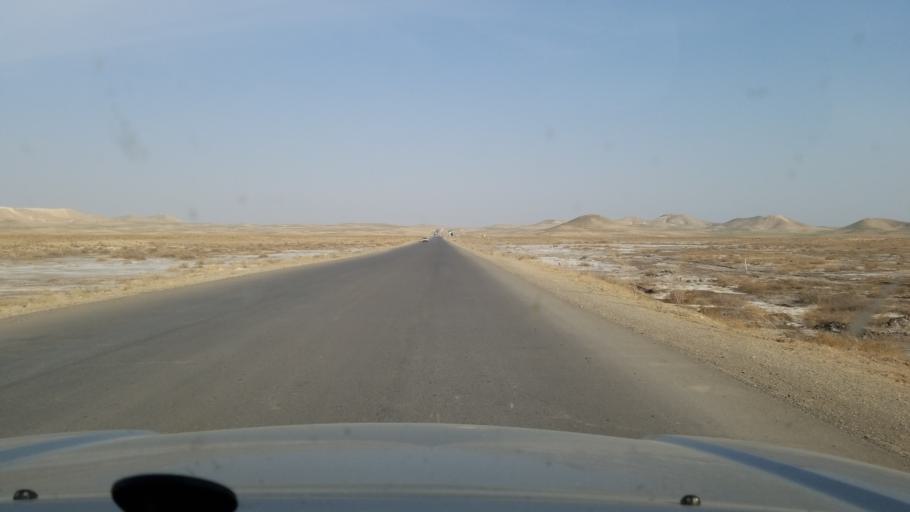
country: AF
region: Jowzjan
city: Khamyab
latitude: 37.6242
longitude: 65.6826
